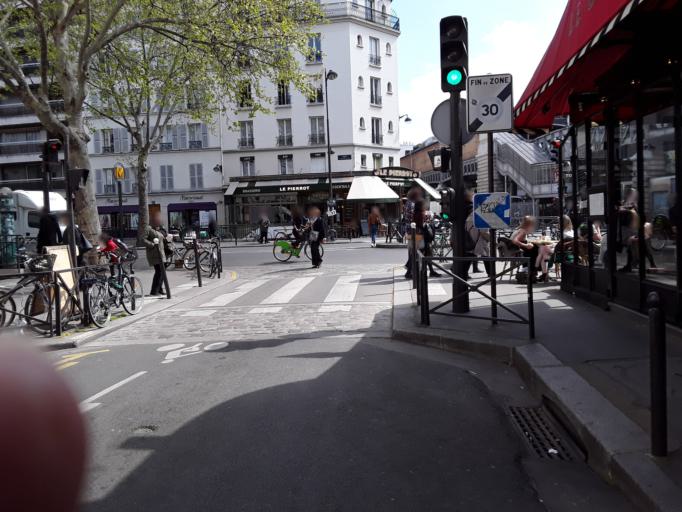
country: FR
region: Ile-de-France
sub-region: Departement des Hauts-de-Seine
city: Vanves
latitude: 48.8494
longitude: 2.2980
